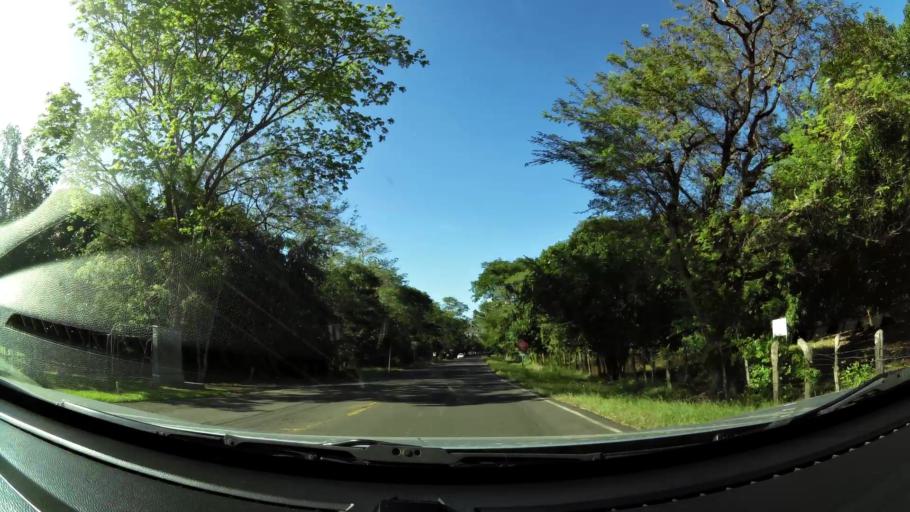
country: CR
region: Guanacaste
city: Sardinal
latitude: 10.5594
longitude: -85.5942
